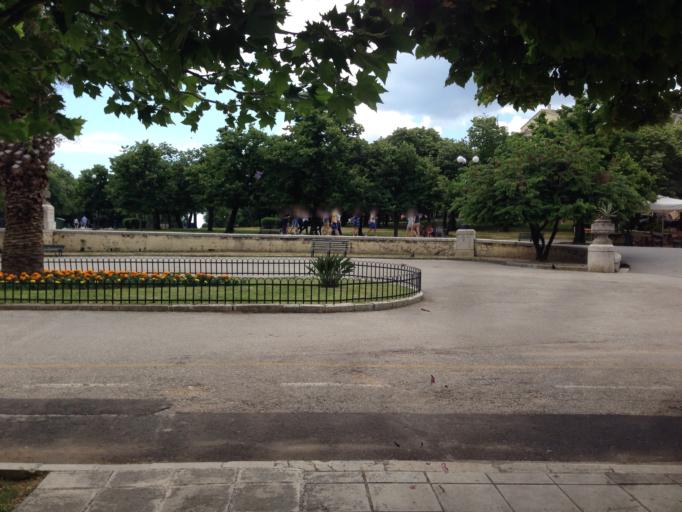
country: GR
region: Ionian Islands
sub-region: Nomos Kerkyras
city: Kerkyra
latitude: 39.6234
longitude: 19.9243
